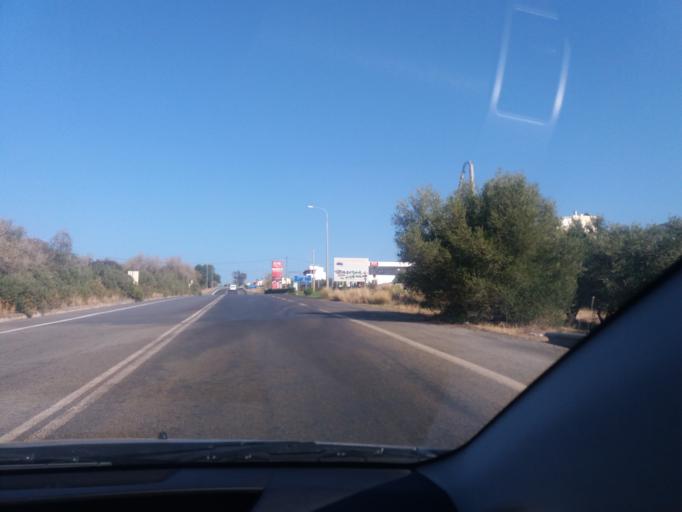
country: GR
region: Crete
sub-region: Nomos Lasithiou
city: Sision
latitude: 35.2908
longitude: 25.5088
